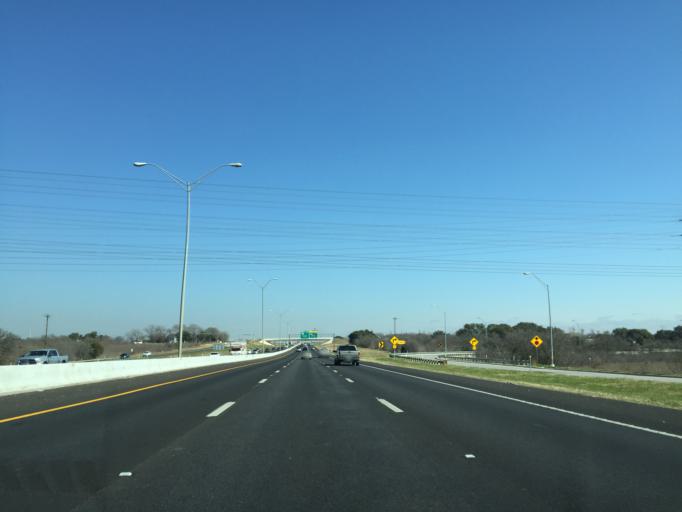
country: US
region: Texas
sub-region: Williamson County
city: Georgetown
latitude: 30.6685
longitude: -97.6677
